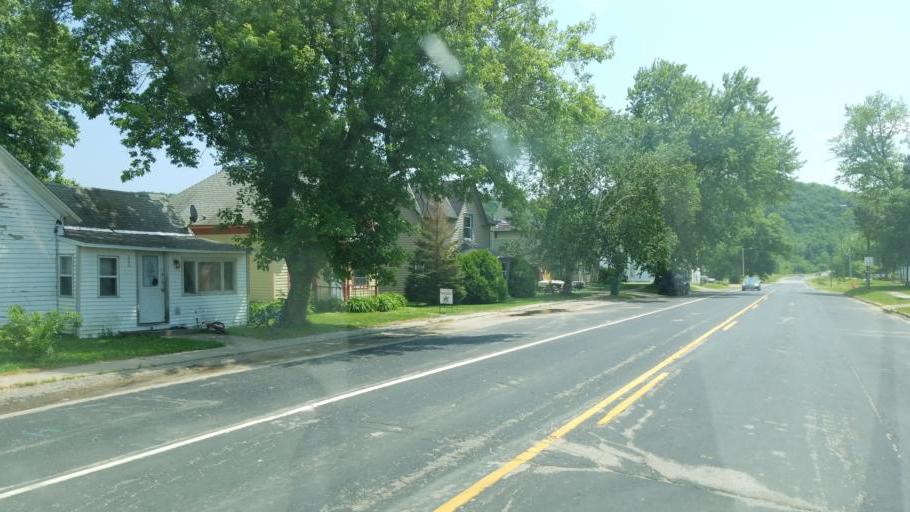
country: US
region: Wisconsin
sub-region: Monroe County
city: Cashton
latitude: 43.5733
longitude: -90.6363
